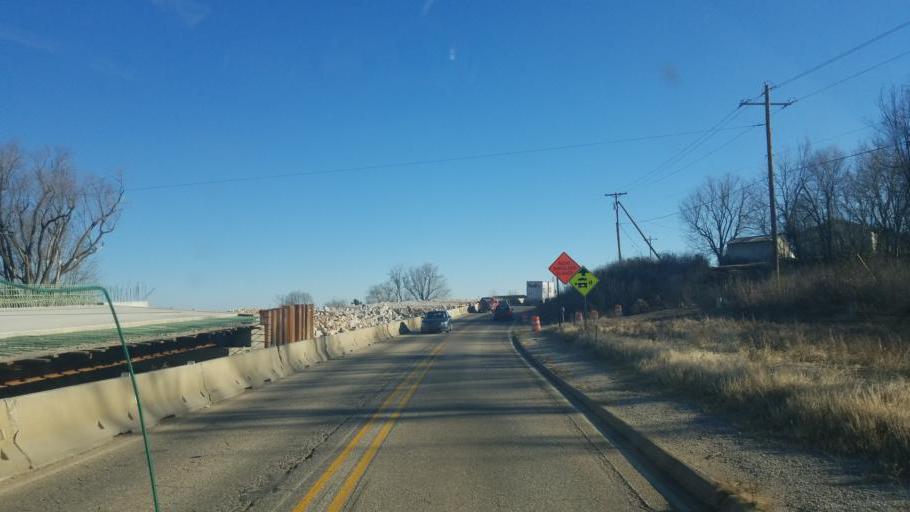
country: US
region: Arkansas
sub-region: Boone County
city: Harrison
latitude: 36.1559
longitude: -92.9925
